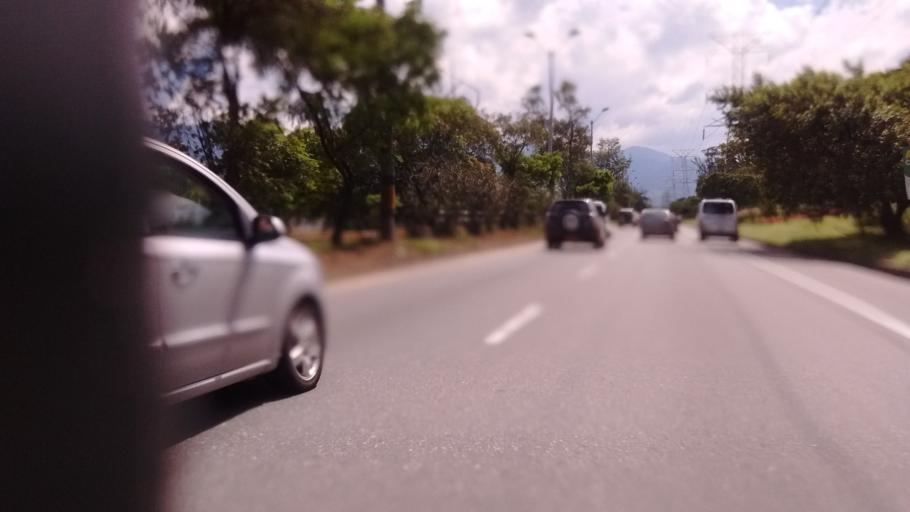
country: CO
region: Antioquia
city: Medellin
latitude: 6.2215
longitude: -75.5774
